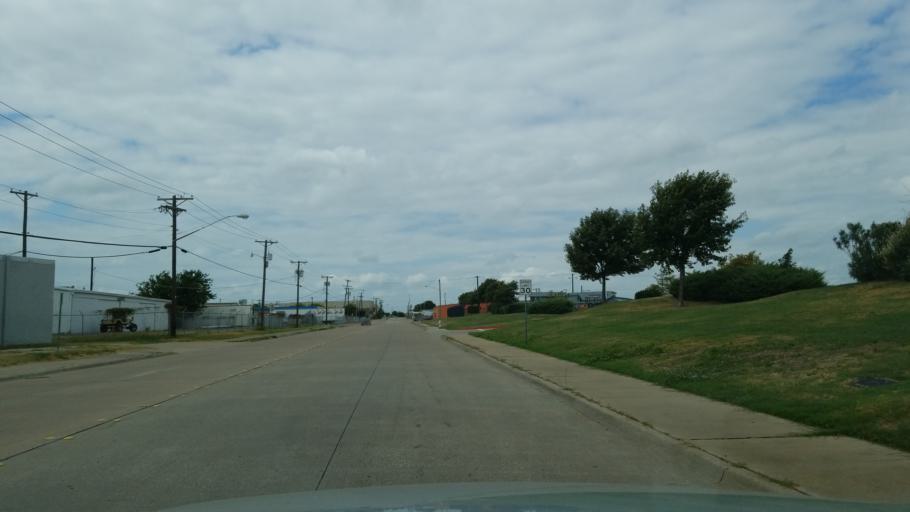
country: US
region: Texas
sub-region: Dallas County
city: Garland
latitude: 32.8866
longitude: -96.6715
